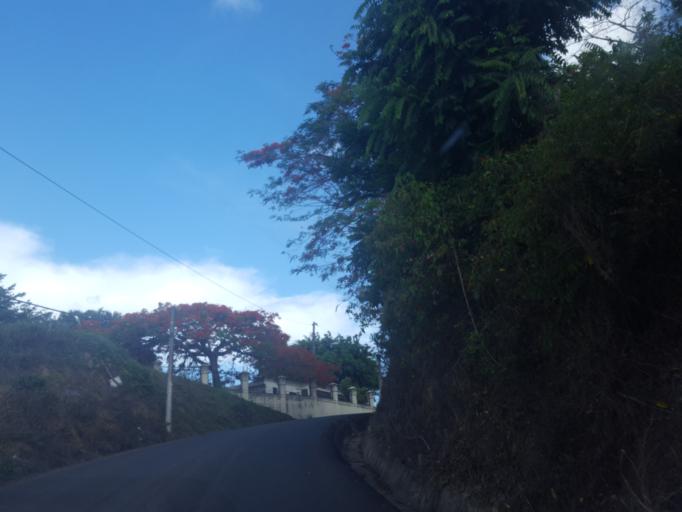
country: DO
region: La Vega
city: Rio Verde Arriba
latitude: 19.3544
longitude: -70.6299
